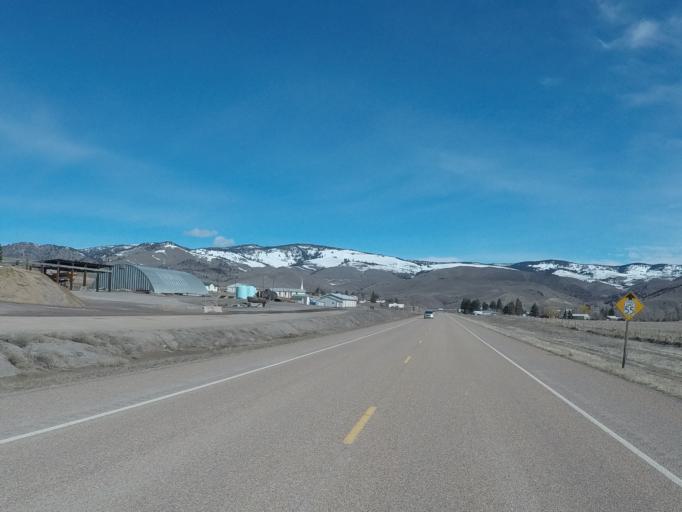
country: US
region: Montana
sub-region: Granite County
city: Philipsburg
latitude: 46.6547
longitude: -113.1601
